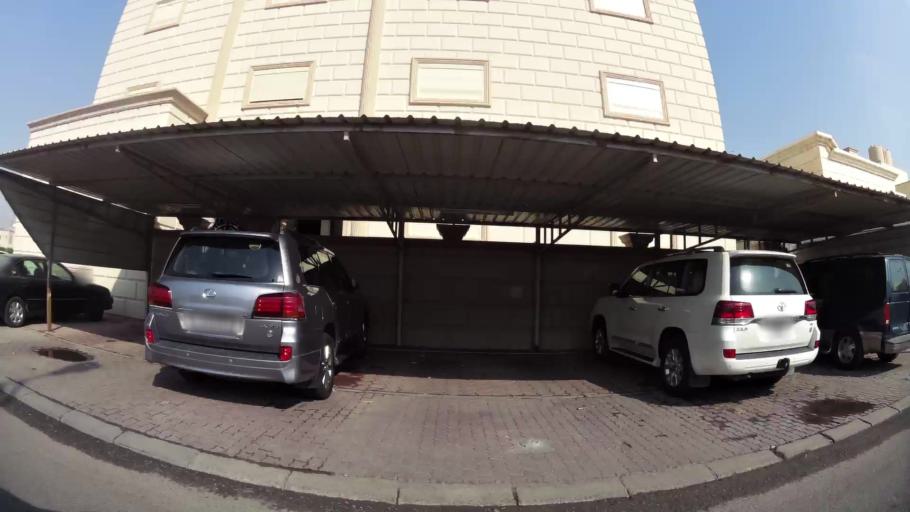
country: KW
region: Al Asimah
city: Ar Rabiyah
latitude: 29.2727
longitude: 47.8956
